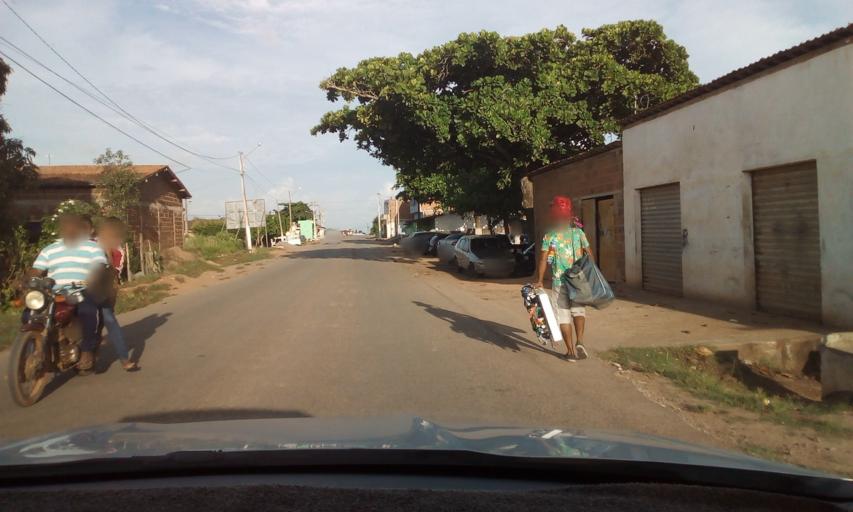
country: BR
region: Pernambuco
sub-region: Gloria Do Goita
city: Gloria do Goita
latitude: -7.9950
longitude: -35.2114
